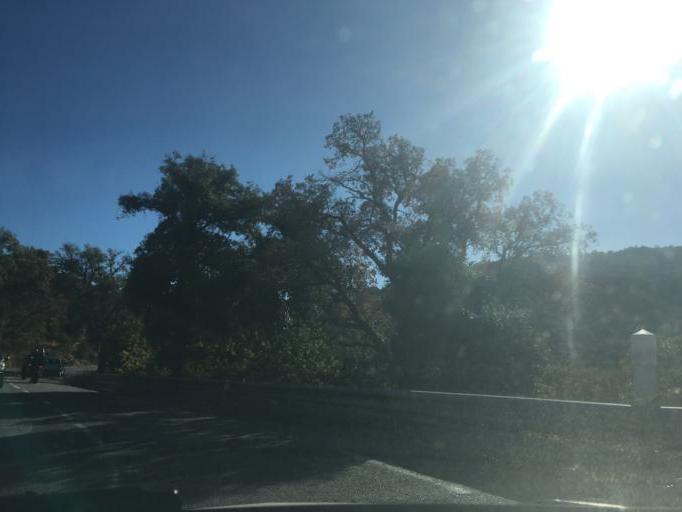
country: FR
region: Provence-Alpes-Cote d'Azur
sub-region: Departement du Var
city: La Garde-Freinet
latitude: 43.3311
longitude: 6.4471
